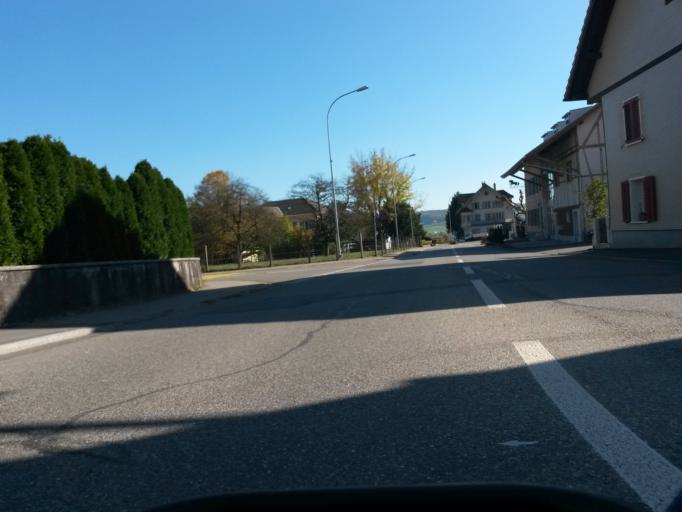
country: CH
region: Solothurn
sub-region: Bezirk Lebern
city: Selzach
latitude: 47.2040
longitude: 7.4567
